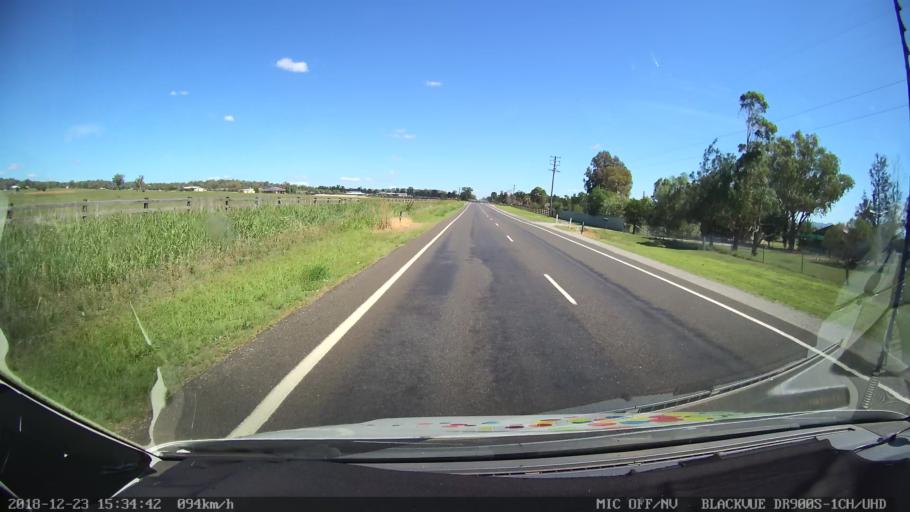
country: AU
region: New South Wales
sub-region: Tamworth Municipality
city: Tamworth
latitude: -31.0175
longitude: 150.8795
